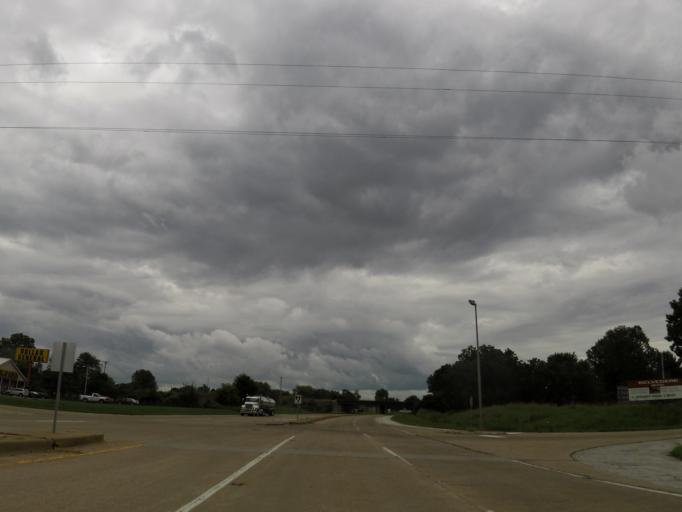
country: US
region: Illinois
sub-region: Alexander County
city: Cairo
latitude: 37.0418
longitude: -89.1951
